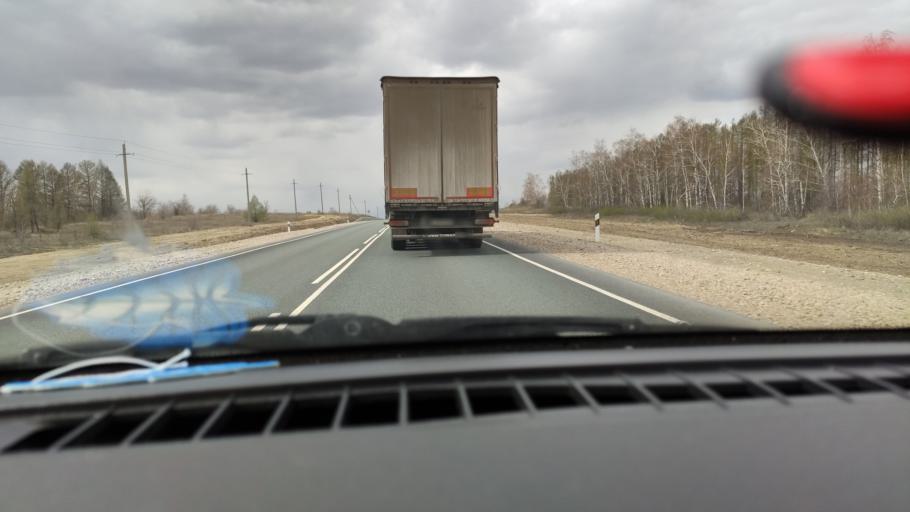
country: RU
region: Saratov
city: Shikhany
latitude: 52.1615
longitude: 47.1123
